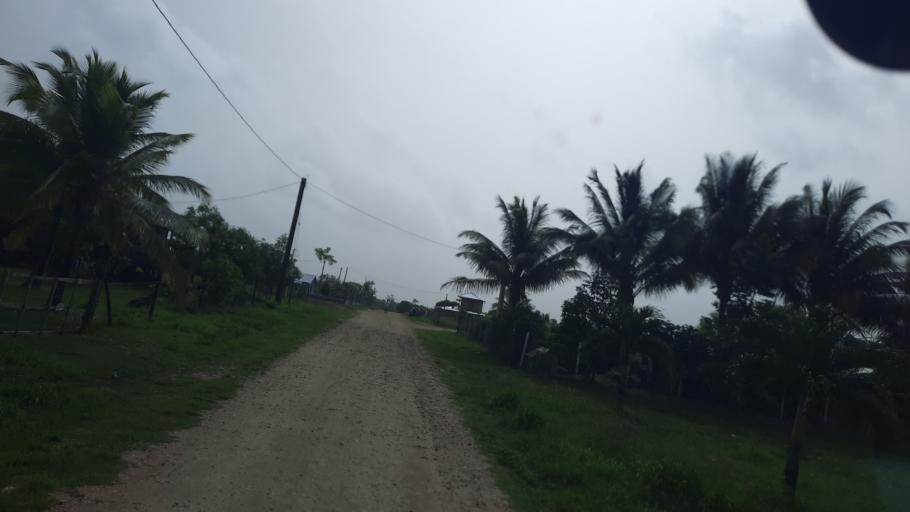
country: BZ
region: Cayo
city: Valley of Peace
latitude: 17.2527
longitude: -88.9395
